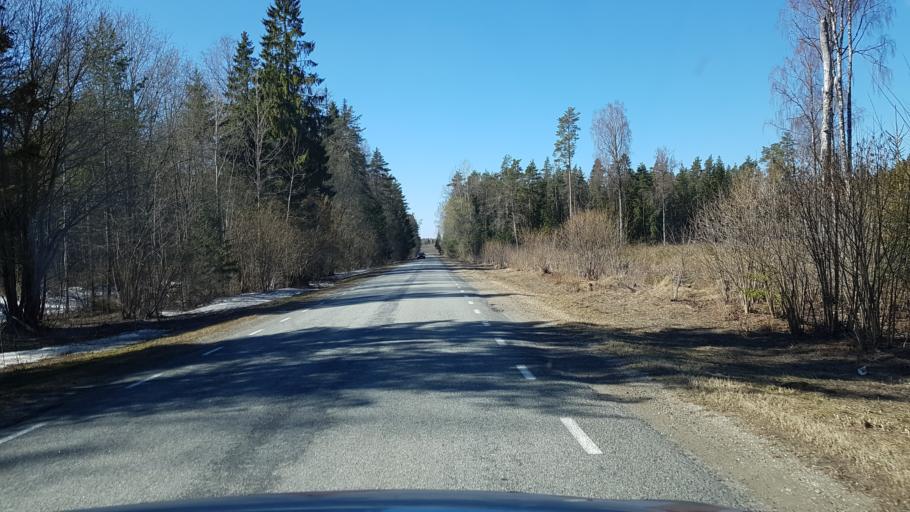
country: EE
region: Laeaene-Virumaa
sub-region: Vaeike-Maarja vald
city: Vaike-Maarja
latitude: 59.1206
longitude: 26.3171
